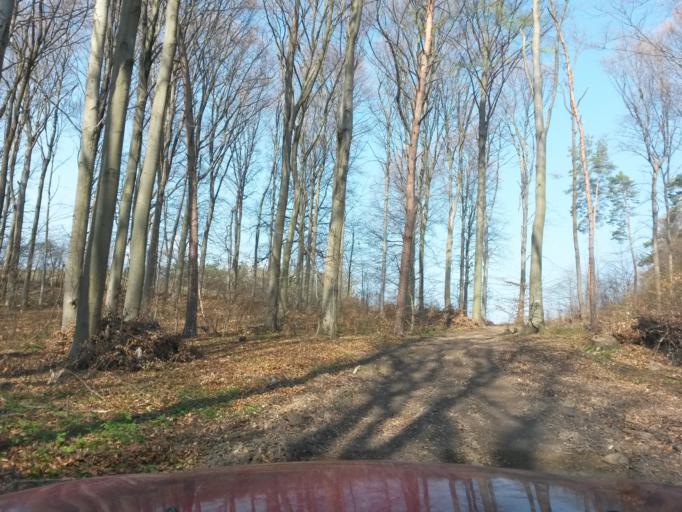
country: SK
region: Presovsky
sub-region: Okres Presov
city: Presov
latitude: 48.9289
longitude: 21.1540
